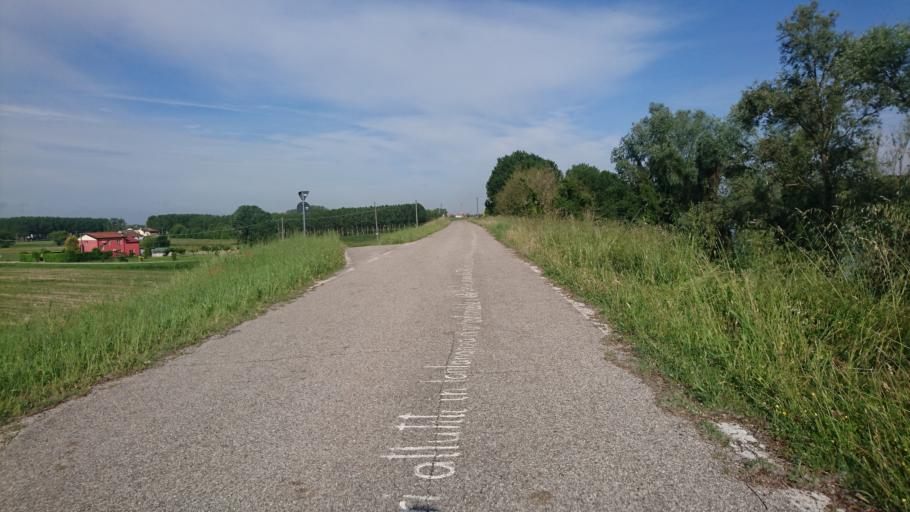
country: IT
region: Veneto
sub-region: Provincia di Rovigo
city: Castelnovo Bariano
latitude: 45.0148
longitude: 11.2808
